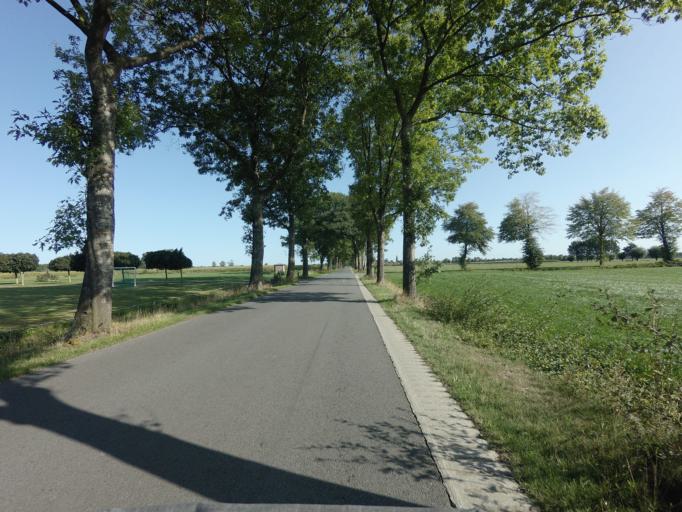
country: NL
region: Overijssel
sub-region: Gemeente Raalte
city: Raalte
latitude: 52.4053
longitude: 6.2842
